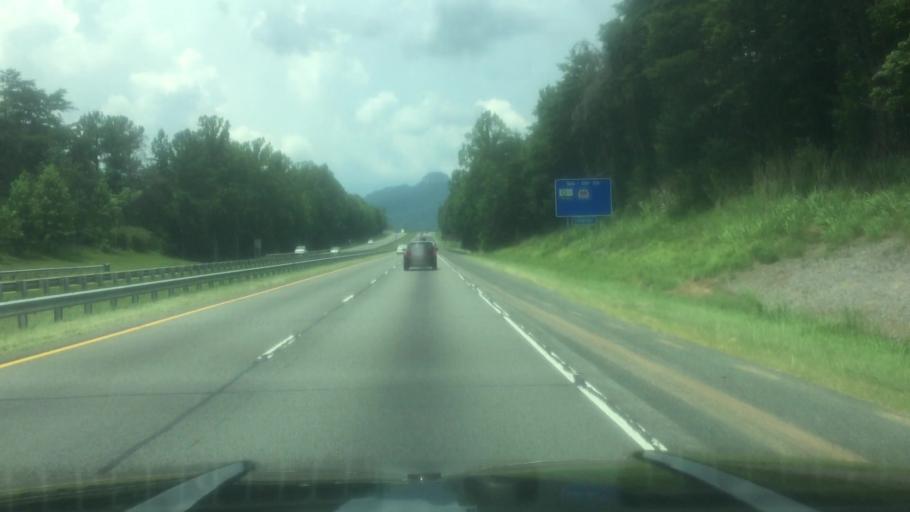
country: US
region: North Carolina
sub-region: Stokes County
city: King
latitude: 36.3110
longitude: -80.4284
